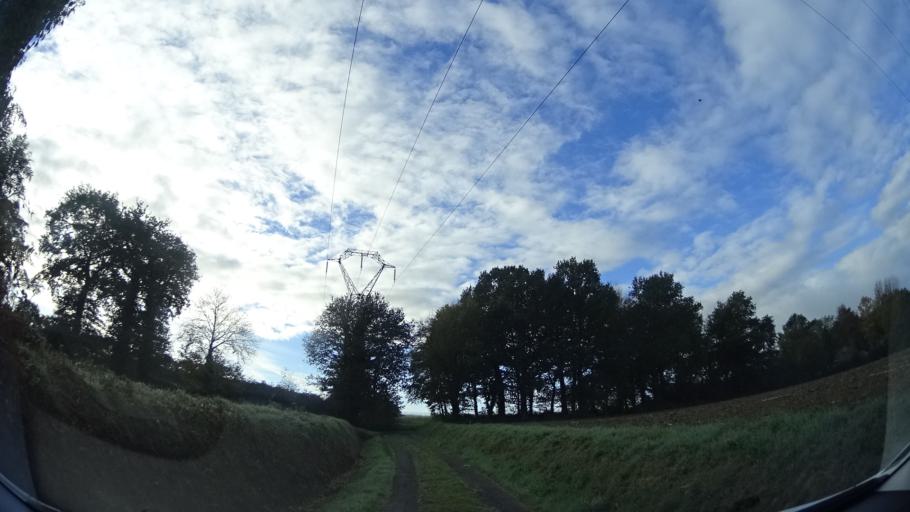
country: FR
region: Brittany
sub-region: Departement d'Ille-et-Vilaine
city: Geveze
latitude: 48.2116
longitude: -1.8057
